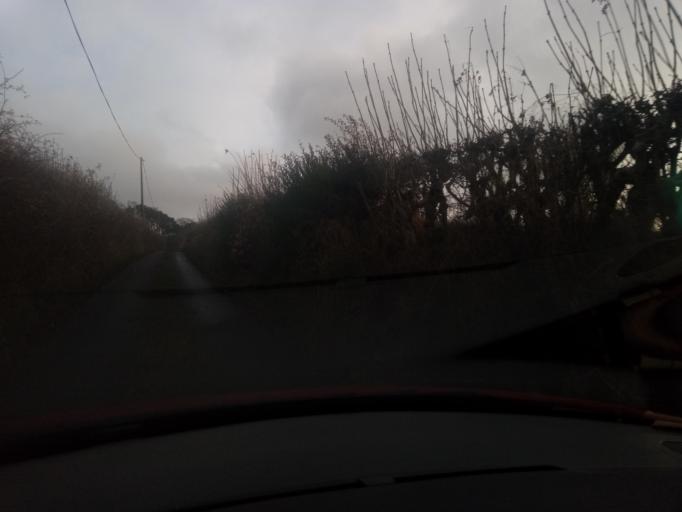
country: GB
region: Scotland
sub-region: The Scottish Borders
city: Jedburgh
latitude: 55.4858
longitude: -2.6107
